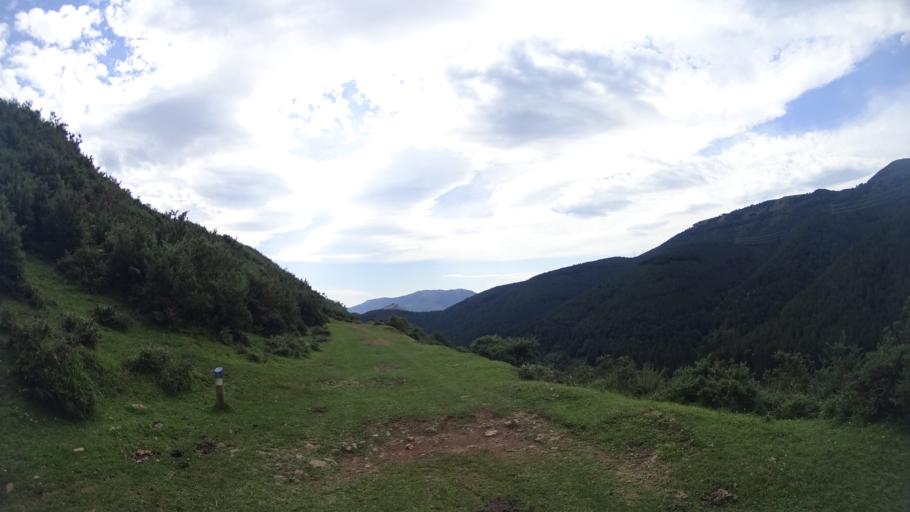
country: ES
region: Basque Country
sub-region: Bizkaia
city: Urtuella
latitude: 43.2811
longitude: -3.0672
